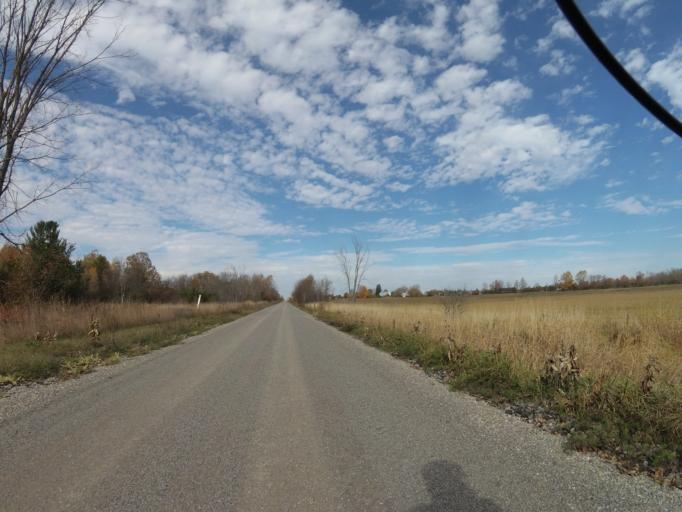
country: CA
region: Ontario
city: Carleton Place
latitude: 45.0386
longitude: -76.0836
